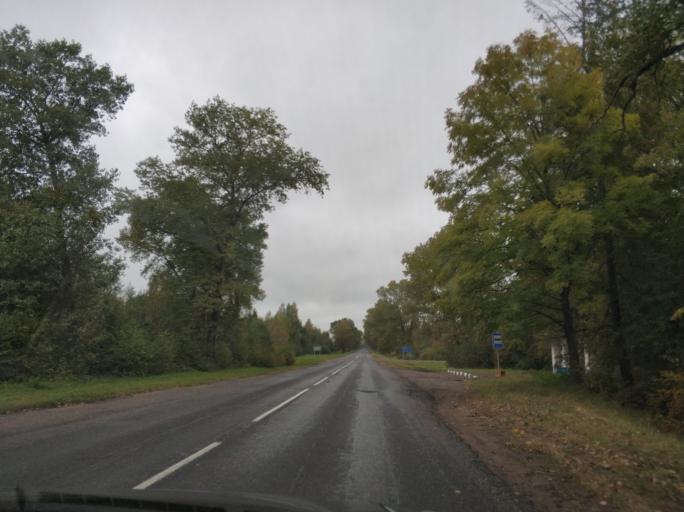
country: BY
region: Vitebsk
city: Polatsk
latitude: 55.4372
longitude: 28.9698
